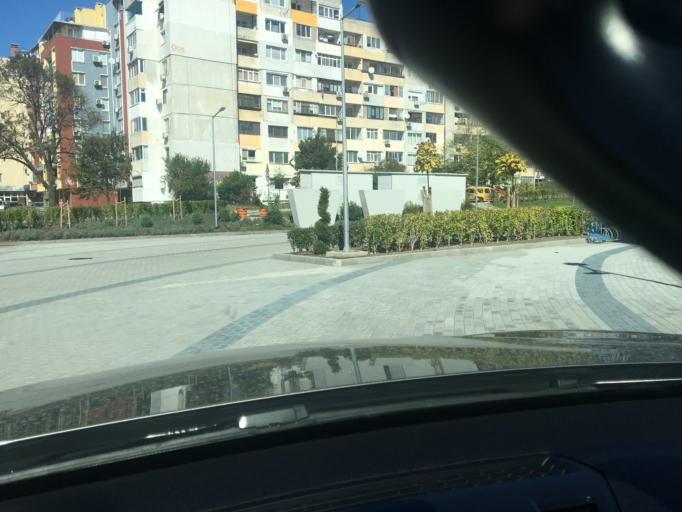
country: BG
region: Burgas
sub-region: Obshtina Burgas
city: Burgas
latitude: 42.5124
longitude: 27.4581
